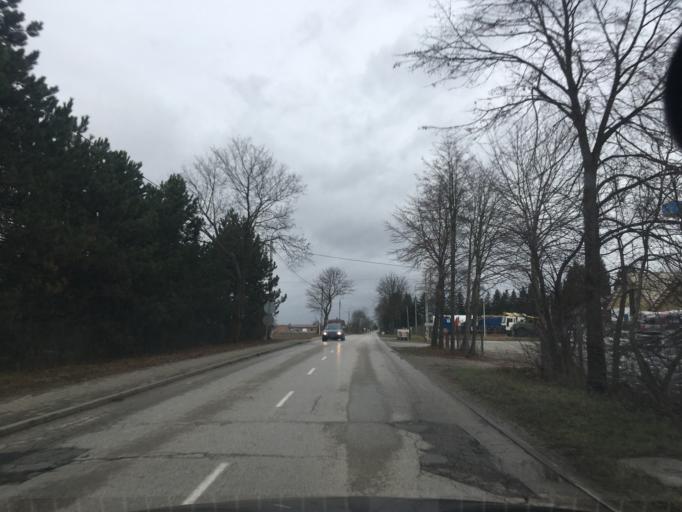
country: PL
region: Masovian Voivodeship
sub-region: Powiat piaseczynski
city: Lesznowola
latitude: 52.1128
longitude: 20.9312
